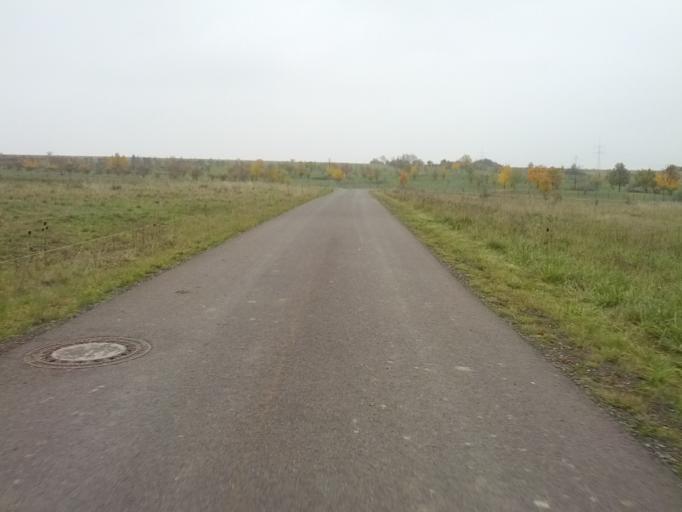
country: DE
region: Thuringia
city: Haina
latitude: 50.9974
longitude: 10.4447
